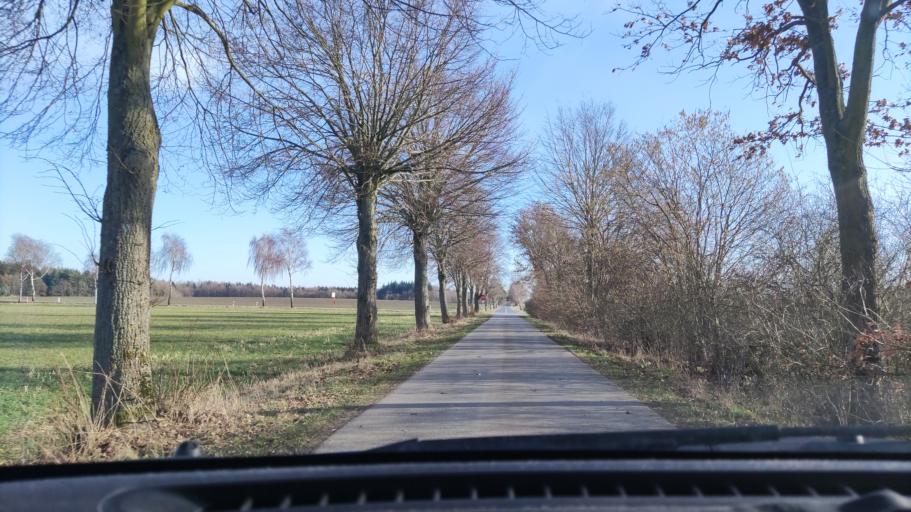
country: DE
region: Lower Saxony
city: Tosterglope
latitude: 53.2142
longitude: 10.8380
